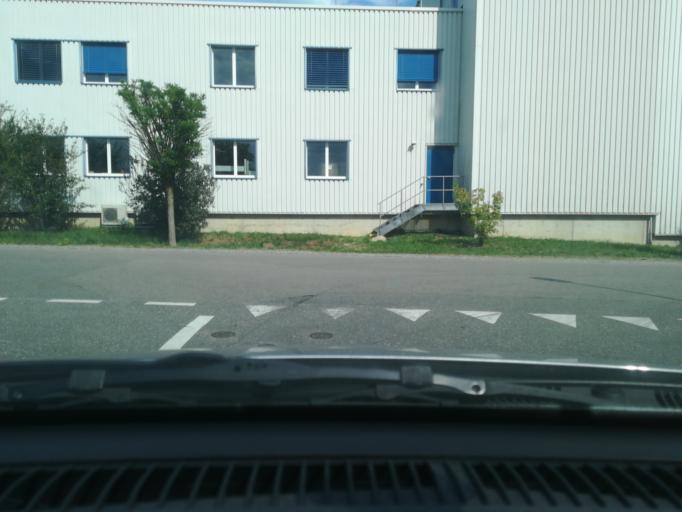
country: CH
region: Schaffhausen
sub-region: Bezirk Reiat
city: Thayngen
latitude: 47.7418
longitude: 8.7165
